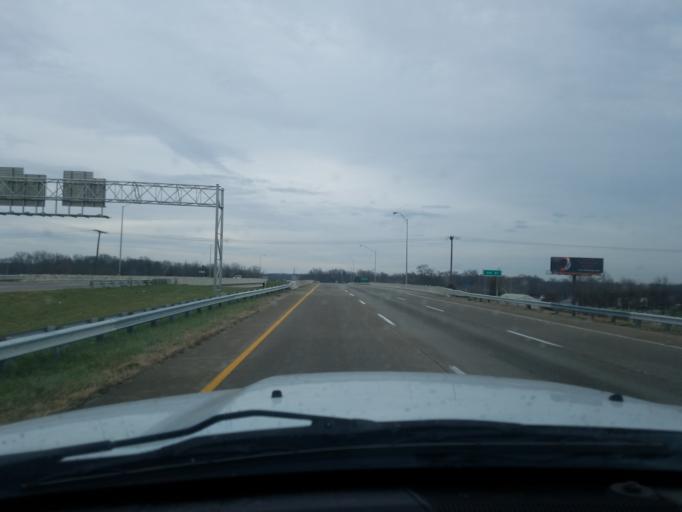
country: US
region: Indiana
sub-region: Clark County
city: Clarksville
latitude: 38.3458
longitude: -85.7483
